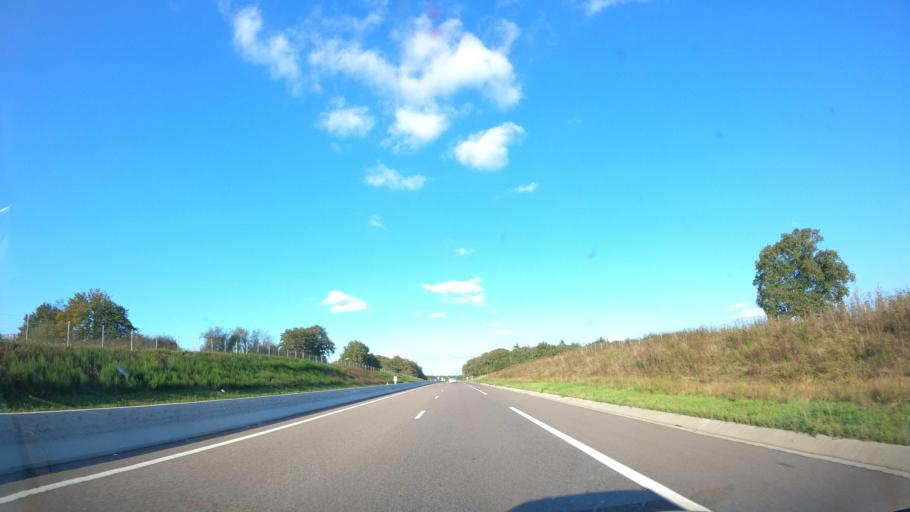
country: FR
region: Bourgogne
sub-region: Departement de Saone-et-Loire
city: Genelard
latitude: 46.5959
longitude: 4.2373
